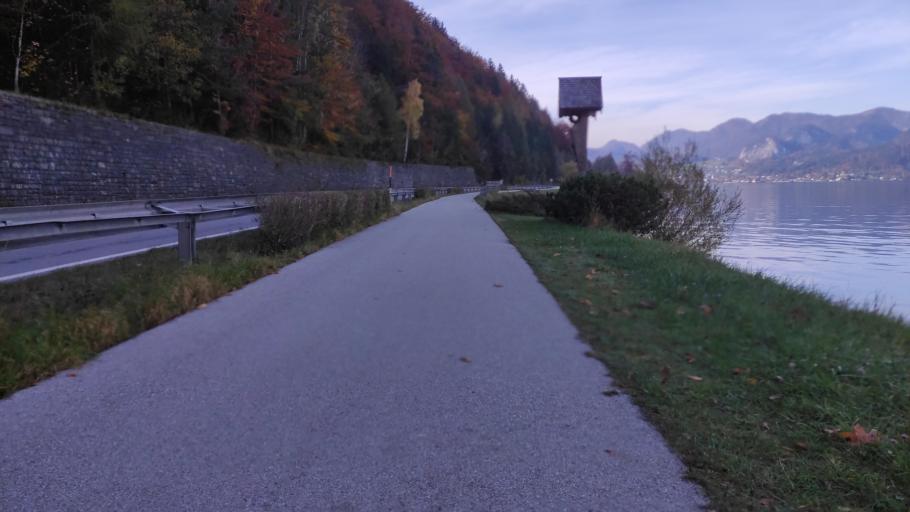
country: AT
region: Salzburg
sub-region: Politischer Bezirk Salzburg-Umgebung
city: Sankt Gilgen
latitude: 47.7391
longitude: 13.3937
